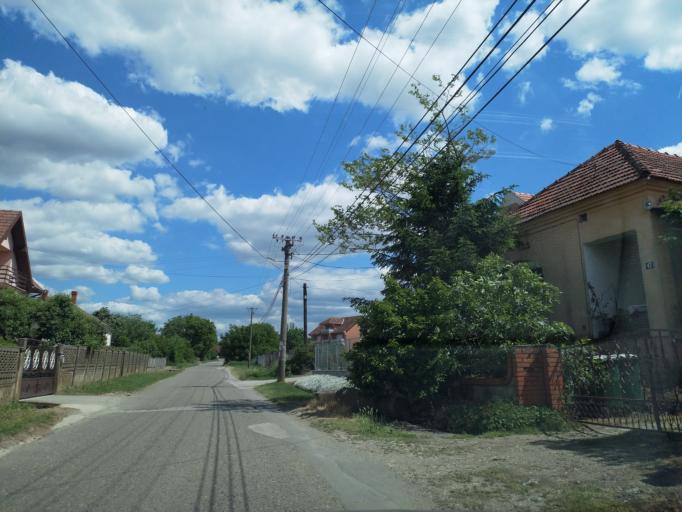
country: RS
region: Central Serbia
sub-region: Pomoravski Okrug
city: Jagodina
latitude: 43.9416
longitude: 21.3006
